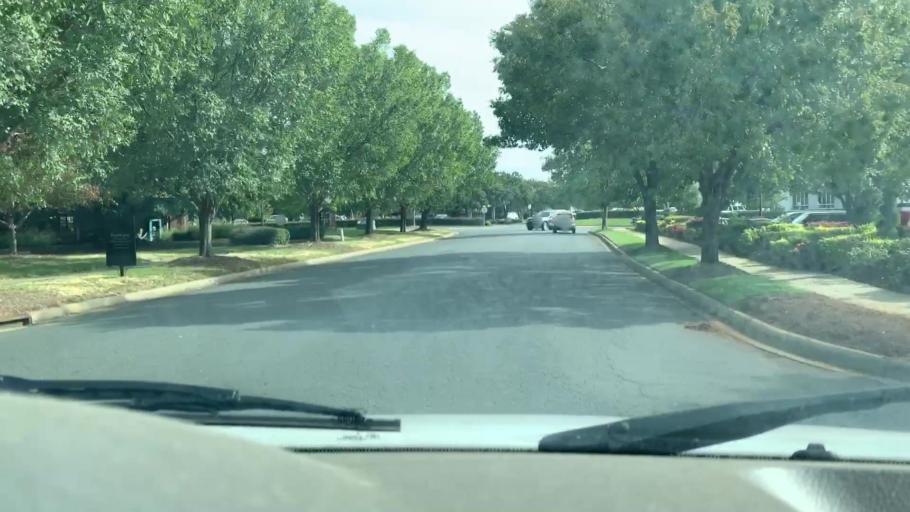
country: US
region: North Carolina
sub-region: Mecklenburg County
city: Cornelius
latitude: 35.4784
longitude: -80.8932
